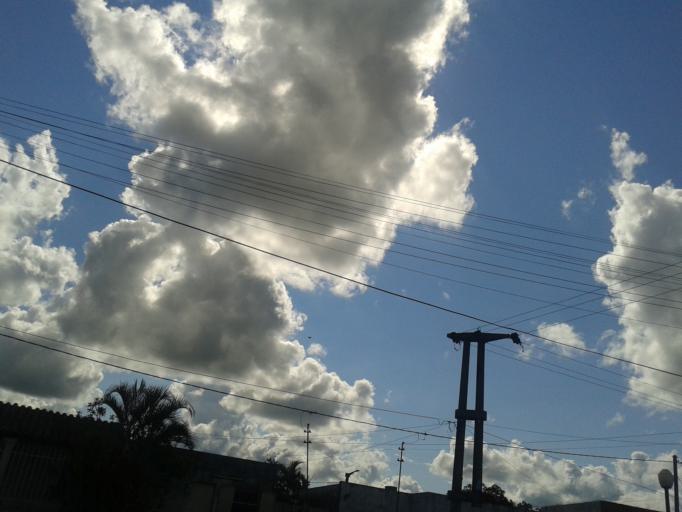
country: AR
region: Formosa
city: Clorinda
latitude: -25.2819
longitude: -57.7356
